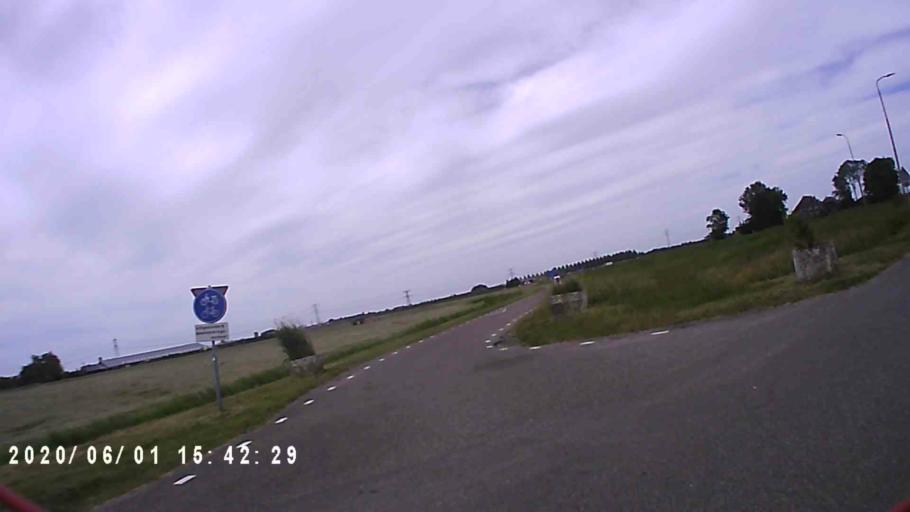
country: NL
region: Friesland
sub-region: Gemeente Boarnsterhim
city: Wergea
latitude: 53.1571
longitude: 5.8269
